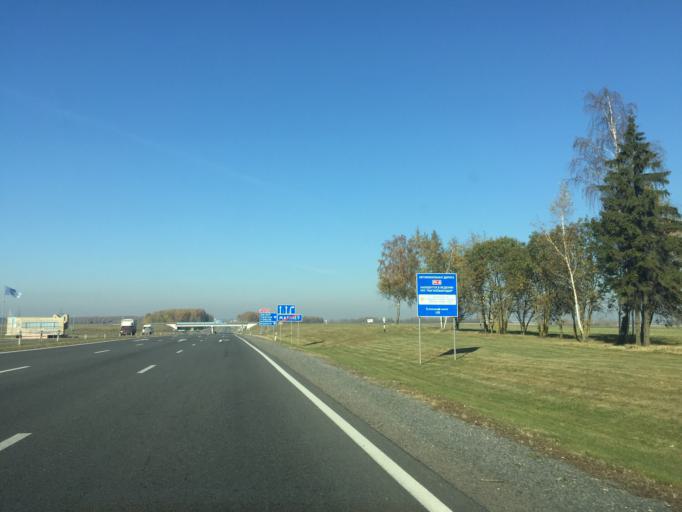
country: BY
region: Mogilev
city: Buynichy
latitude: 53.9465
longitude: 30.2285
